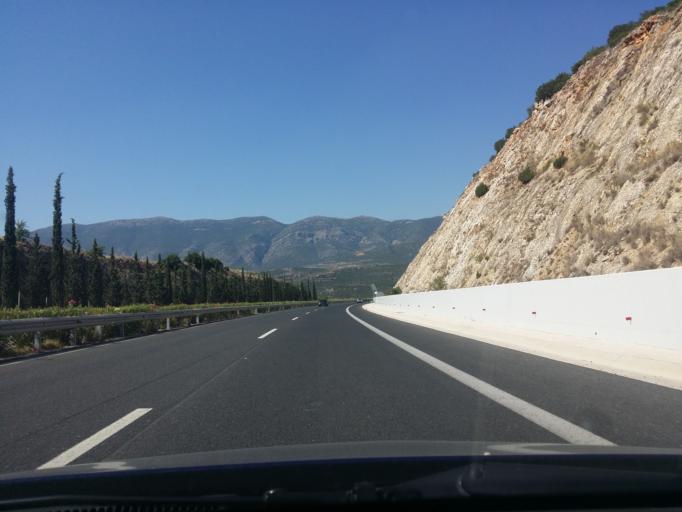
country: GR
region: Peloponnese
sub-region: Nomos Korinthias
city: Nemea
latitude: 37.7308
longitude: 22.6219
